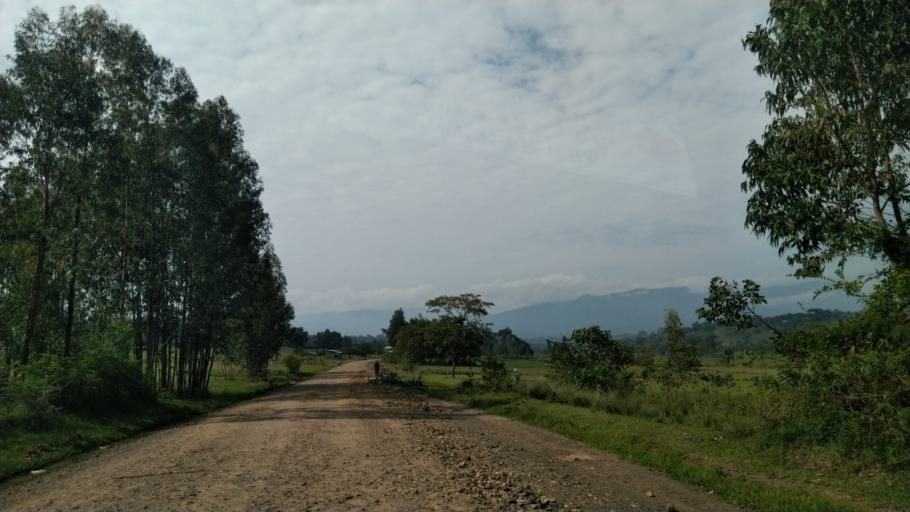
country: ET
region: Oromiya
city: Jima
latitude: 7.6763
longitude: 37.2408
